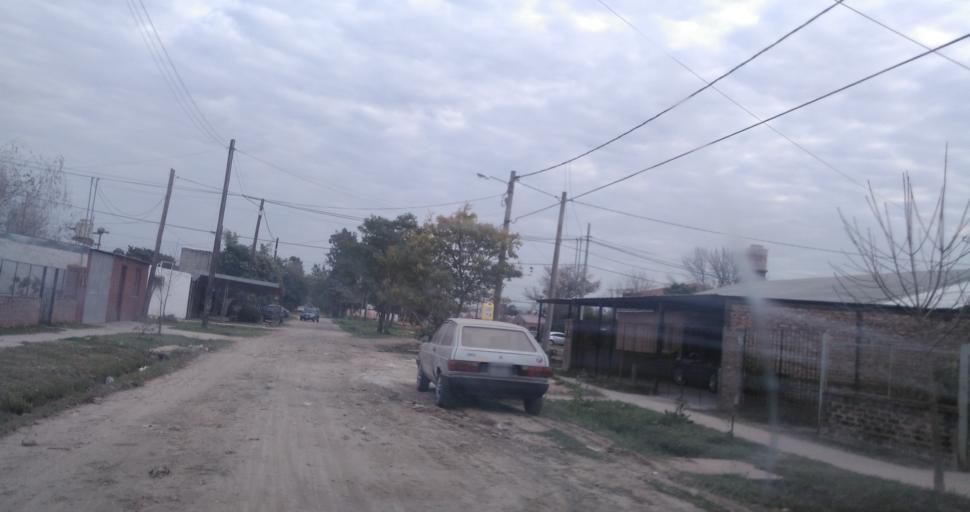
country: AR
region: Chaco
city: Fontana
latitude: -27.4481
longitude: -59.0349
